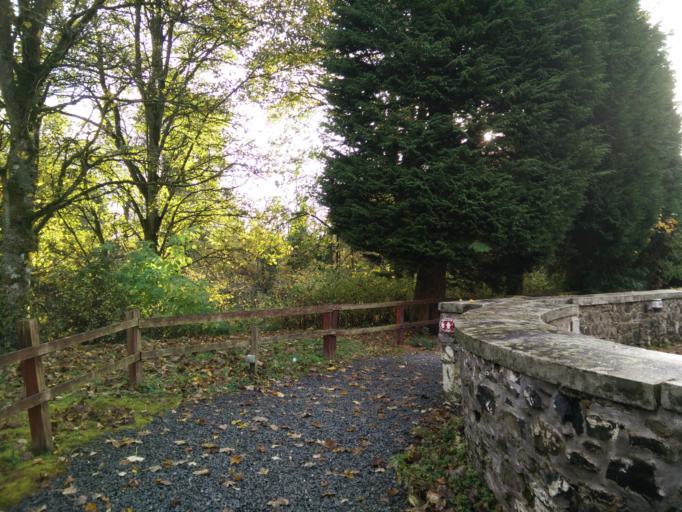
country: GB
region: Scotland
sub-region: The Scottish Borders
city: Peebles
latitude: 55.7128
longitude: -3.2162
